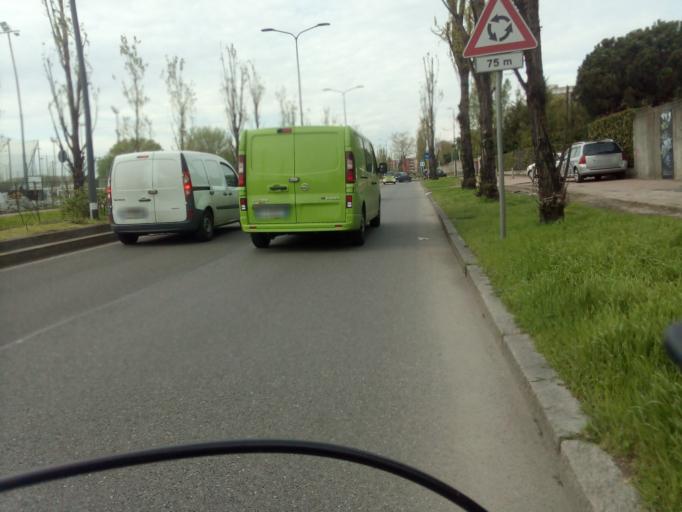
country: IT
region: Lombardy
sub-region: Citta metropolitana di Milano
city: Cesano Boscone
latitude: 45.4651
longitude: 9.1134
